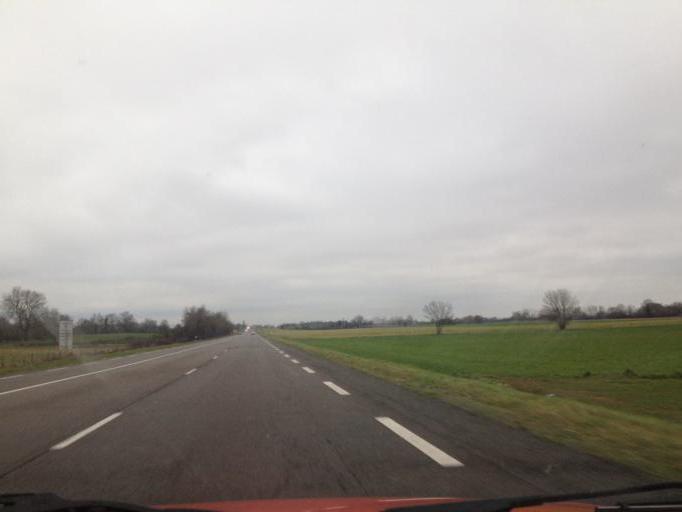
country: FR
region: Auvergne
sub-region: Departement de l'Allier
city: Toulon-sur-Allier
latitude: 46.4867
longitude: 3.3653
